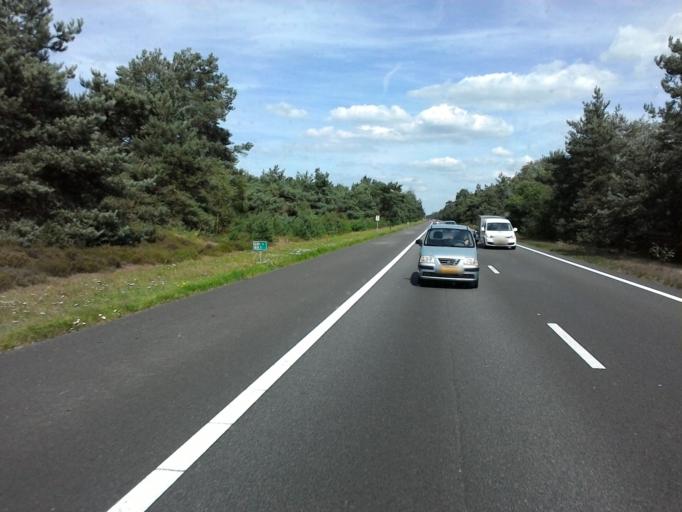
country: NL
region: Gelderland
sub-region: Gemeente Elburg
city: Elburg
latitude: 52.3917
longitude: 5.8513
